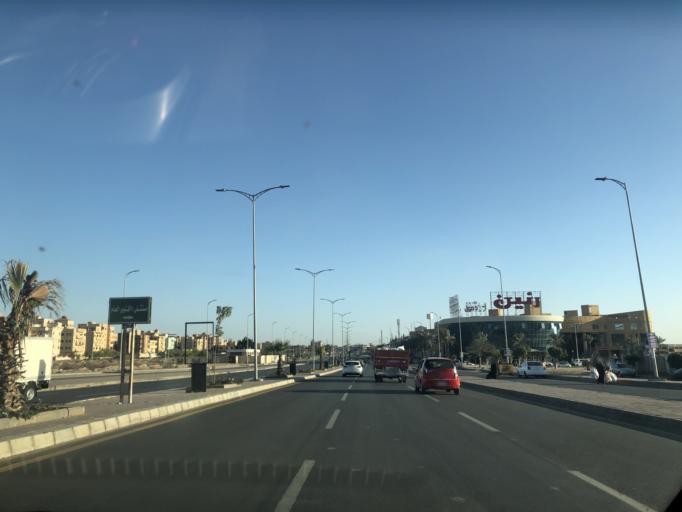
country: EG
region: Al Jizah
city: Madinat Sittah Uktubar
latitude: 29.9501
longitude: 30.9127
